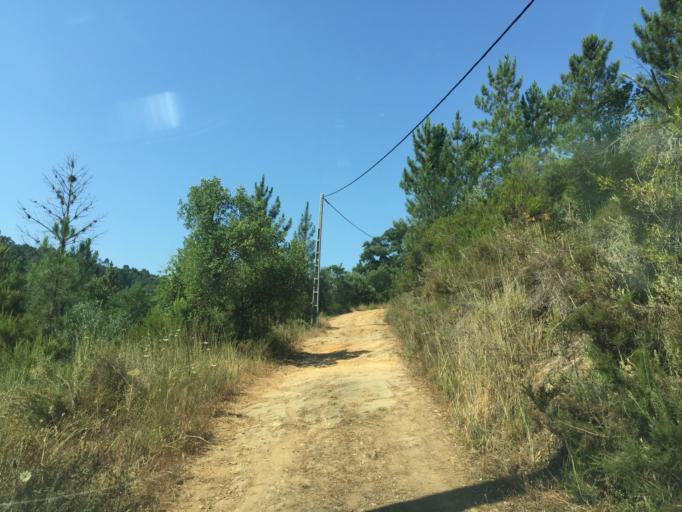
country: PT
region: Santarem
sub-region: Ferreira do Zezere
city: Ferreira do Zezere
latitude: 39.6048
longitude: -8.2789
